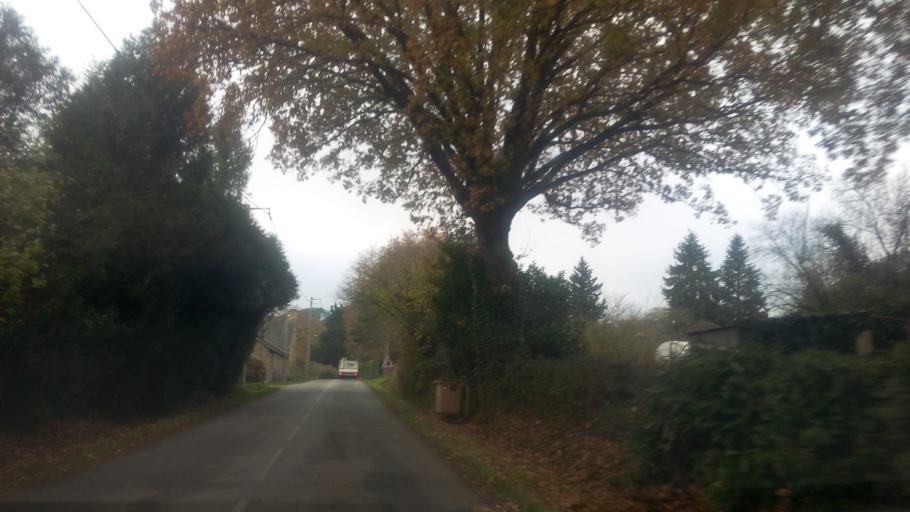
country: FR
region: Brittany
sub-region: Departement du Morbihan
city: Saint-Jean-la-Poterie
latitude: 47.6542
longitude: -2.1248
